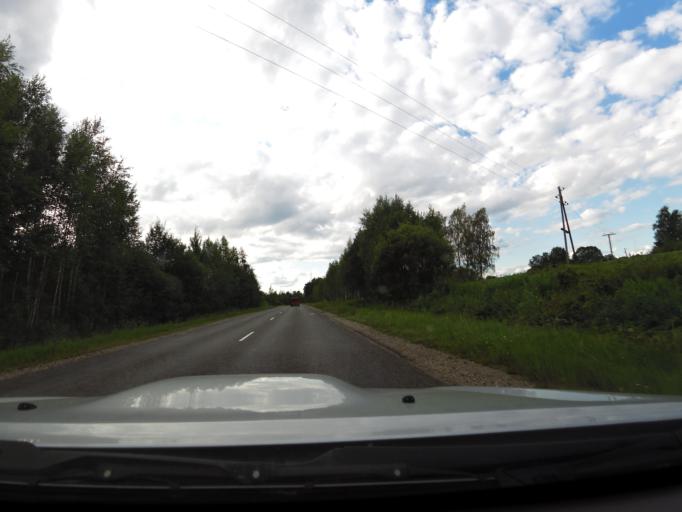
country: LV
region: Akniste
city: Akniste
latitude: 56.0090
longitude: 25.9374
